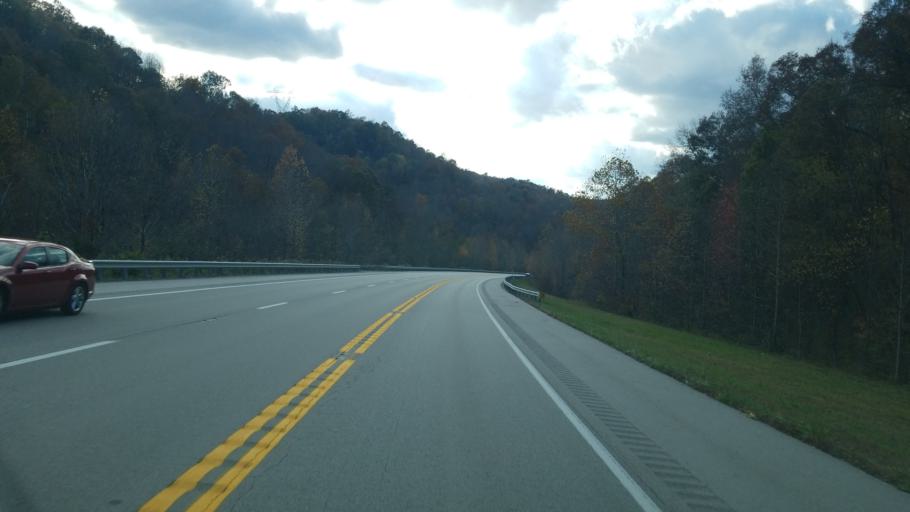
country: US
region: Kentucky
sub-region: Lewis County
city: Vanceburg
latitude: 38.5744
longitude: -83.3098
